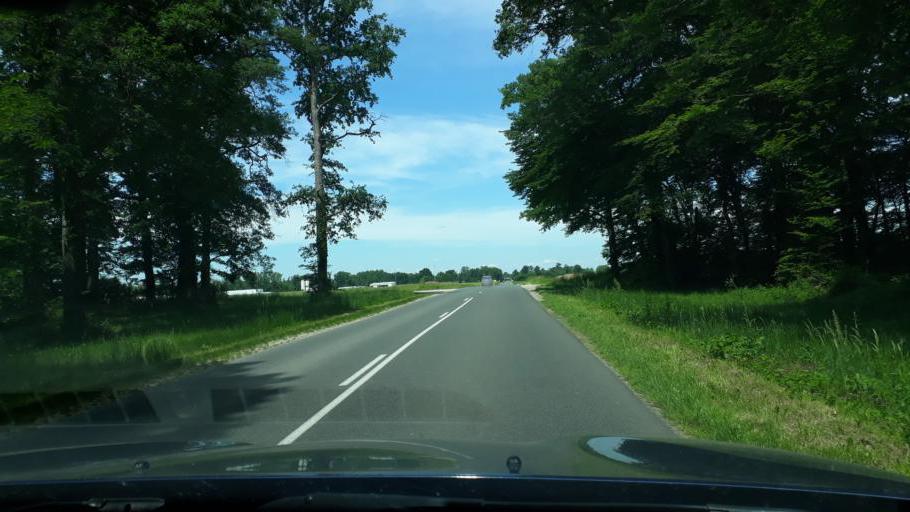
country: FR
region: Centre
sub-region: Departement du Loiret
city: Boiscommun
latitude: 48.0390
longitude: 2.3062
